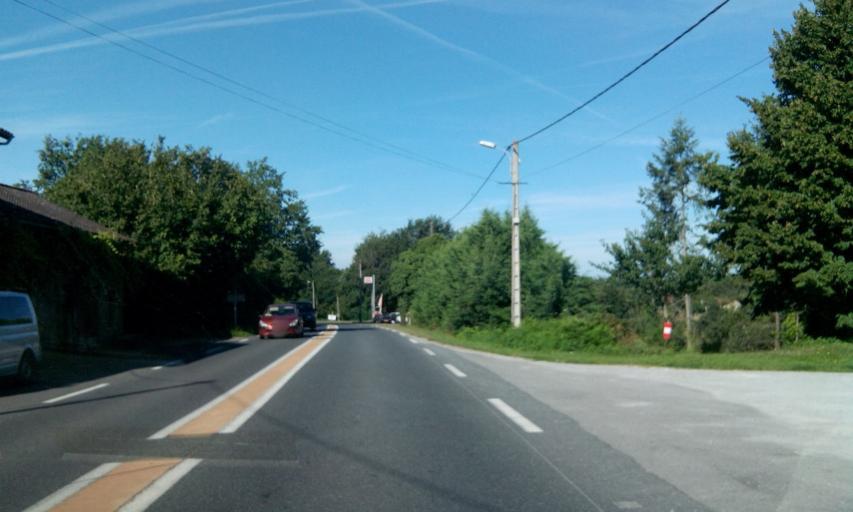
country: FR
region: Limousin
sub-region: Departement de la Haute-Vienne
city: Saint-Just-le-Martel
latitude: 45.8487
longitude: 1.4287
